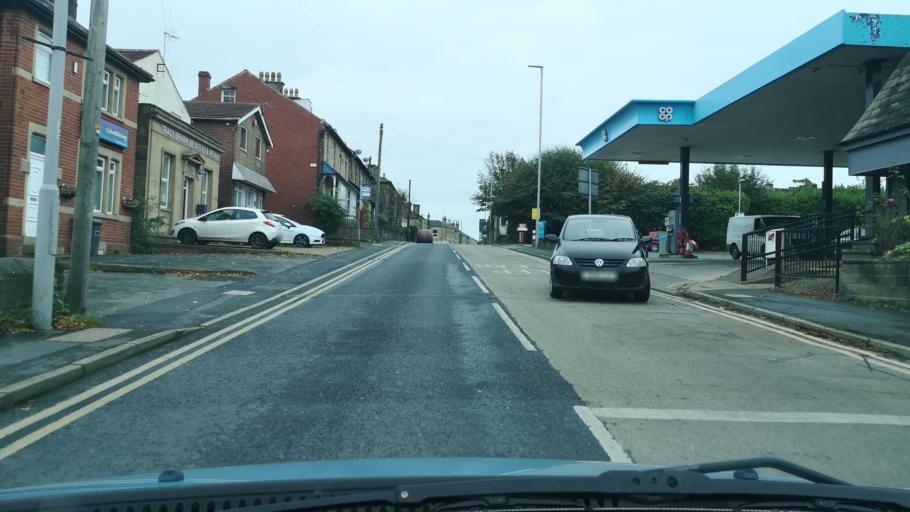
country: GB
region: England
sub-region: Kirklees
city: Heckmondwike
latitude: 53.7296
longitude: -1.6837
